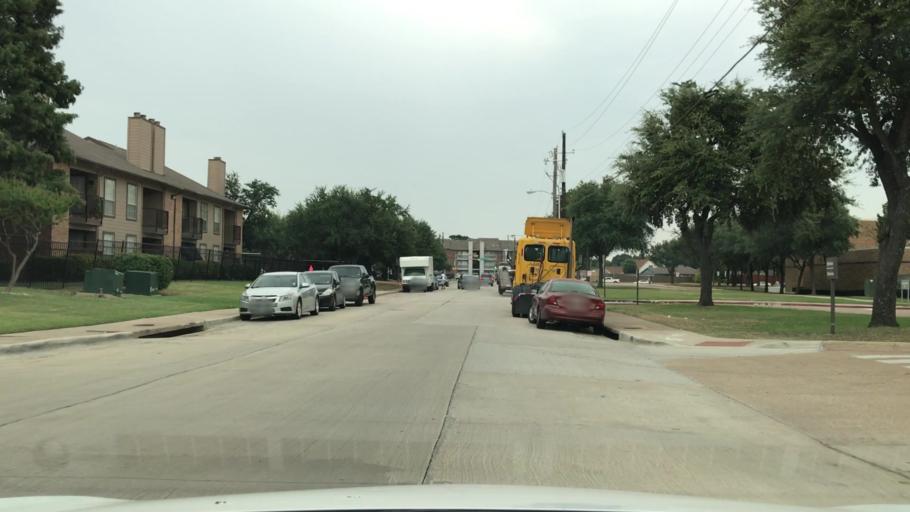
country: US
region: Texas
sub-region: Dallas County
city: Carrollton
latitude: 32.9991
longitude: -96.8686
